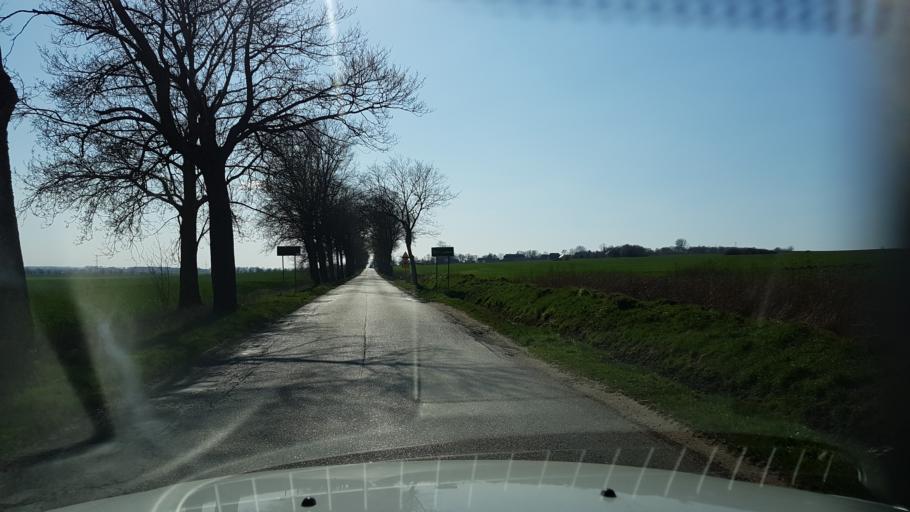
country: PL
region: West Pomeranian Voivodeship
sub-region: Powiat slawienski
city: Darlowo
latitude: 54.4592
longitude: 16.5058
